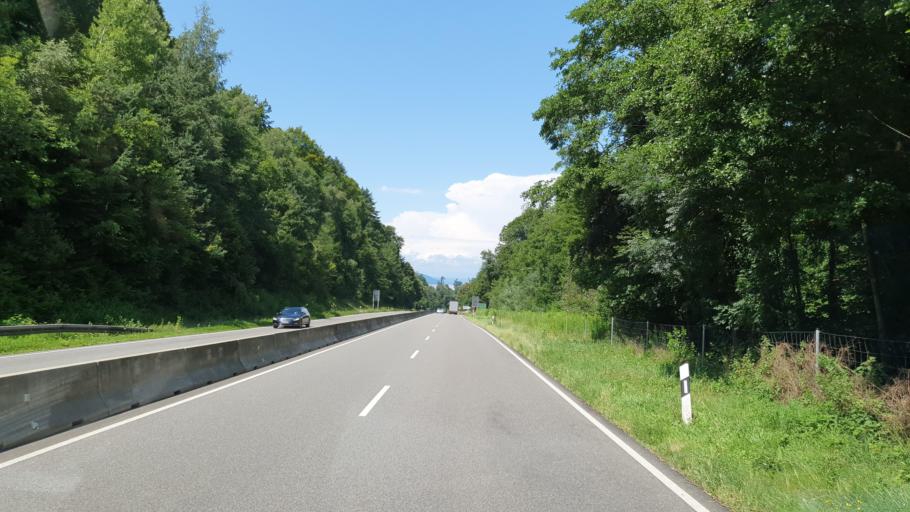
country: DE
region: Baden-Wuerttemberg
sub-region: Tuebingen Region
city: Uhldingen-Muhlhofen
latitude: 47.7179
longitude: 9.2487
